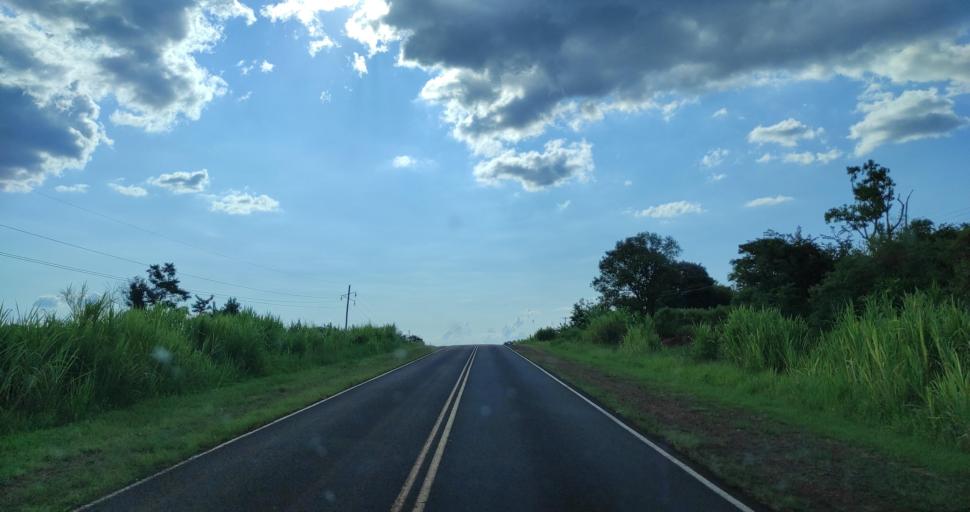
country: AR
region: Misiones
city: San Vicente
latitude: -26.3507
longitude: -54.1915
